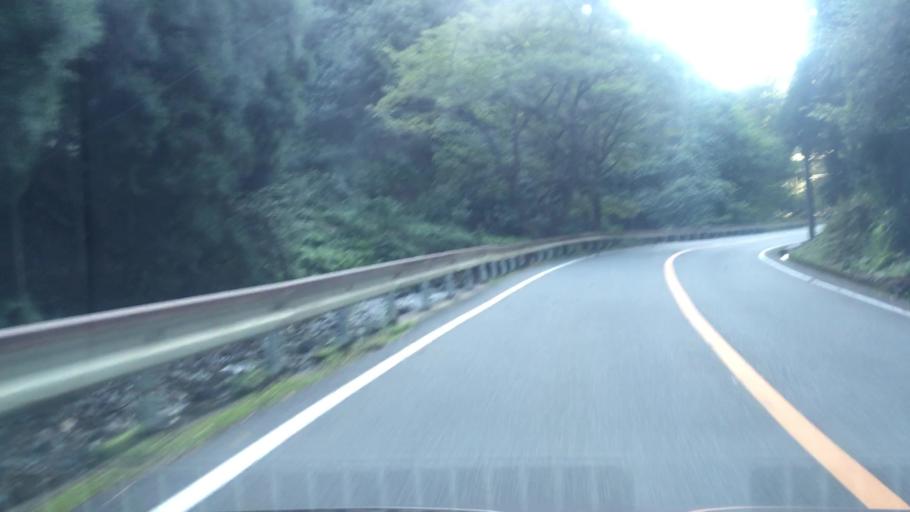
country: JP
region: Hyogo
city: Toyooka
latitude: 35.6165
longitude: 134.8577
